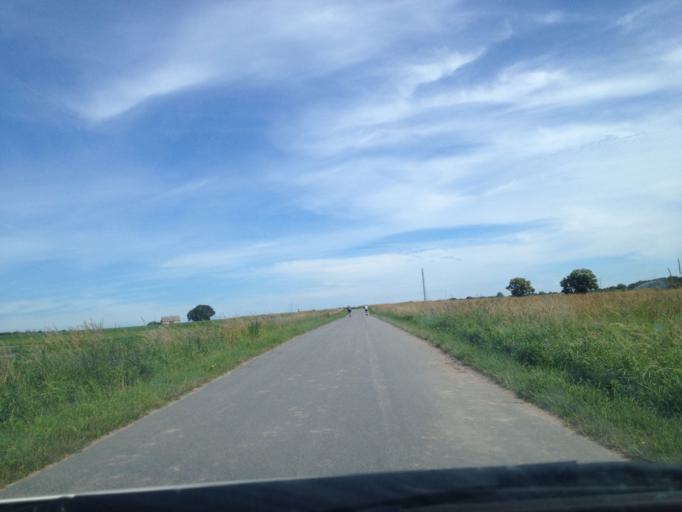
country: DK
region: Central Jutland
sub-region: Samso Kommune
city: Tranebjerg
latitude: 55.9395
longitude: 10.5546
